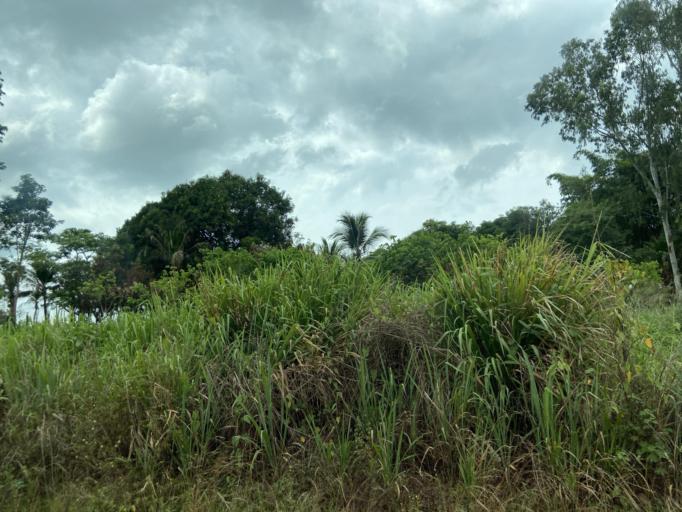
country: BR
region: Para
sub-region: Maraba
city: Maraba
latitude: -5.2728
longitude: -49.0201
